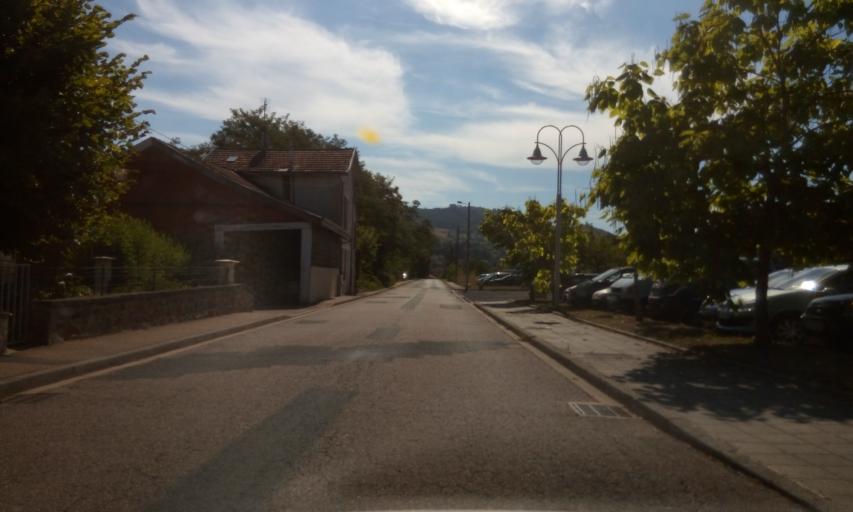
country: FR
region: Rhone-Alpes
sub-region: Departement du Rhone
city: Amplepuis
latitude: 45.9712
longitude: 4.3274
